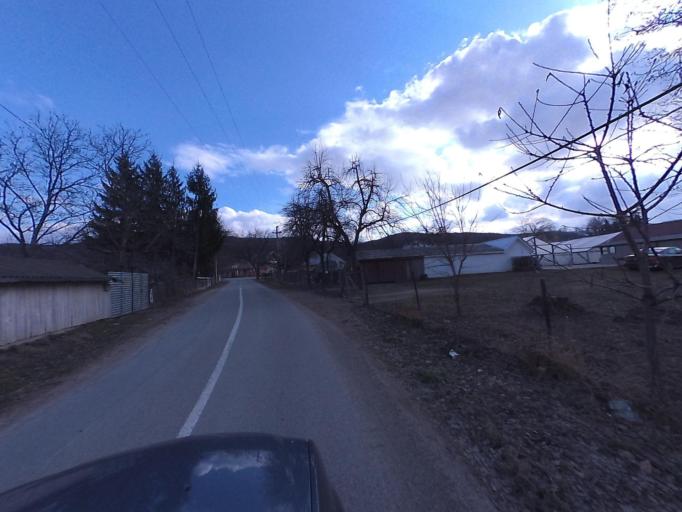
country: RO
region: Neamt
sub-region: Comuna Grumazesti
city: Topolita
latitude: 47.1976
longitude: 26.4076
